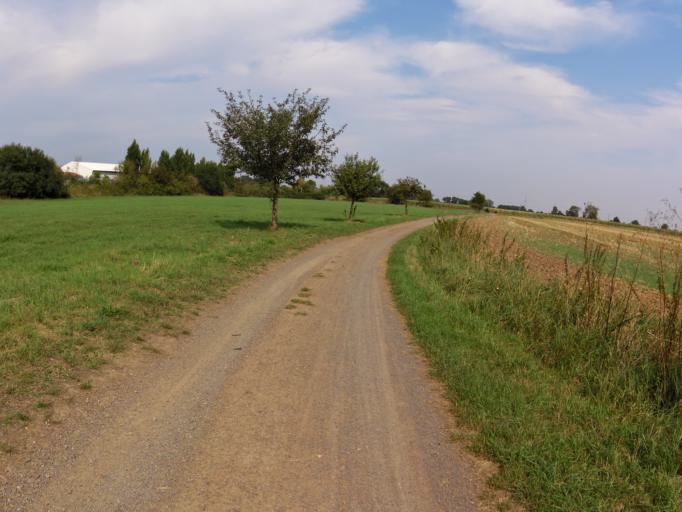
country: DE
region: Lower Saxony
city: Stolzenau
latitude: 52.5241
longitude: 9.0811
